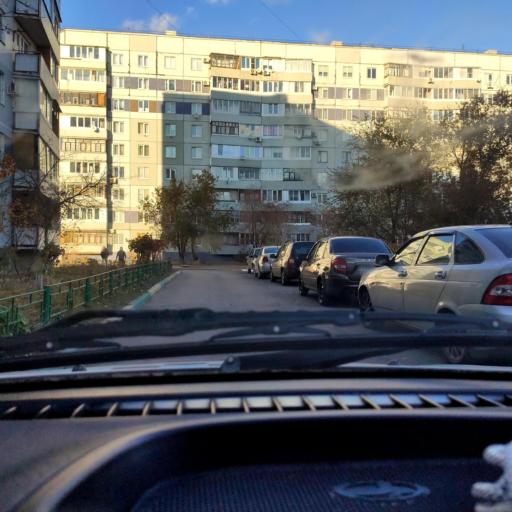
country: RU
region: Samara
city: Zhigulevsk
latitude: 53.4827
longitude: 49.5180
